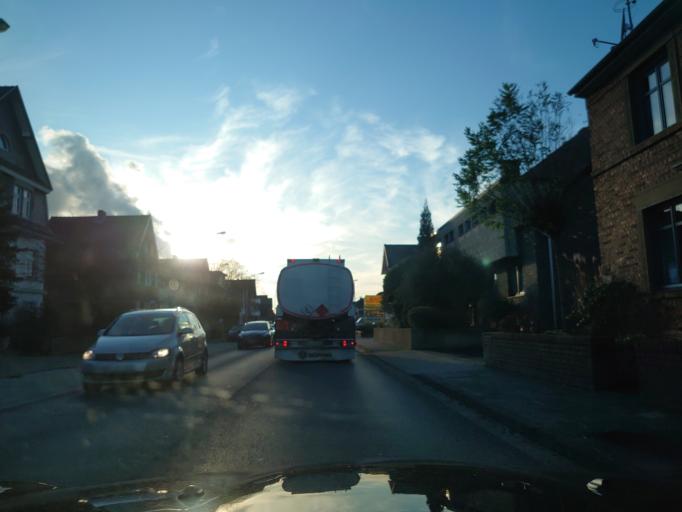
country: DE
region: North Rhine-Westphalia
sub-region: Regierungsbezirk Dusseldorf
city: Rommerskirchen
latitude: 51.0385
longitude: 6.7001
